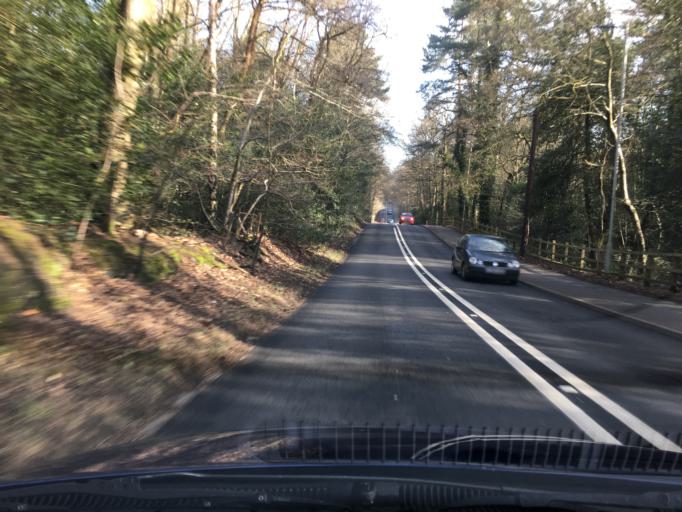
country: GB
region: England
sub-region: Bracknell Forest
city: Crowthorne
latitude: 51.3583
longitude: -0.7985
